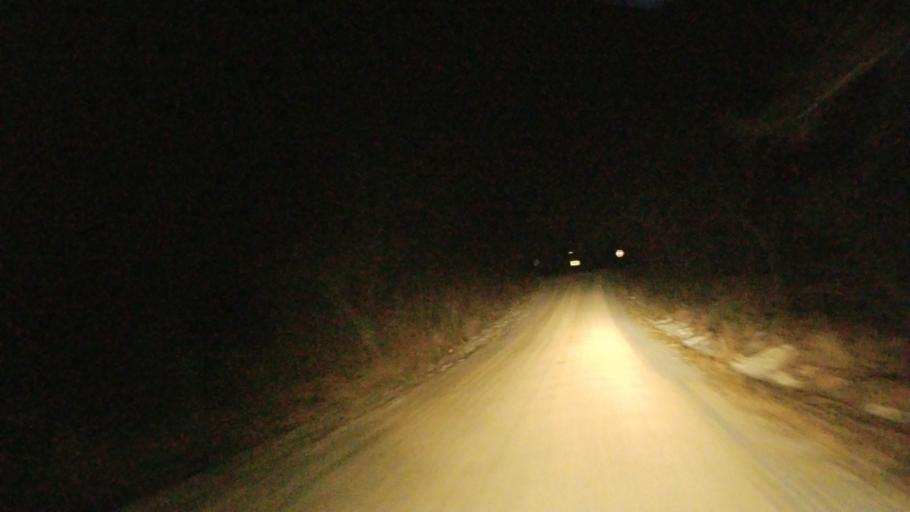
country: US
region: Michigan
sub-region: Osceola County
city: Reed City
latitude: 43.8516
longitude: -85.3838
